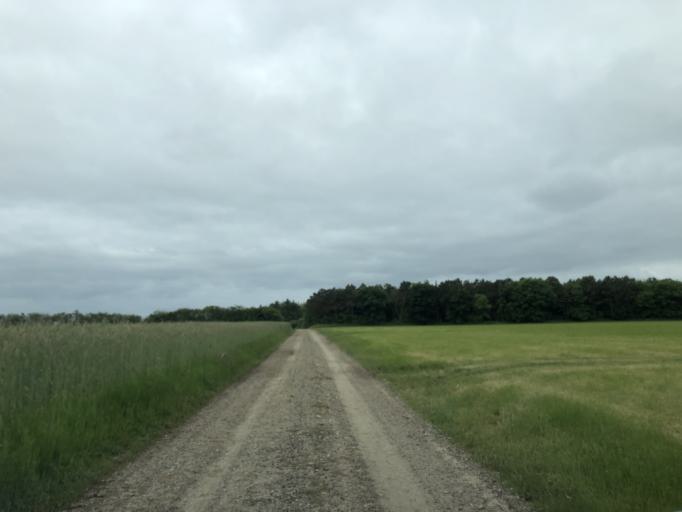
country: DK
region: Central Jutland
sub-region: Holstebro Kommune
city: Ulfborg
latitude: 56.2281
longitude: 8.1741
